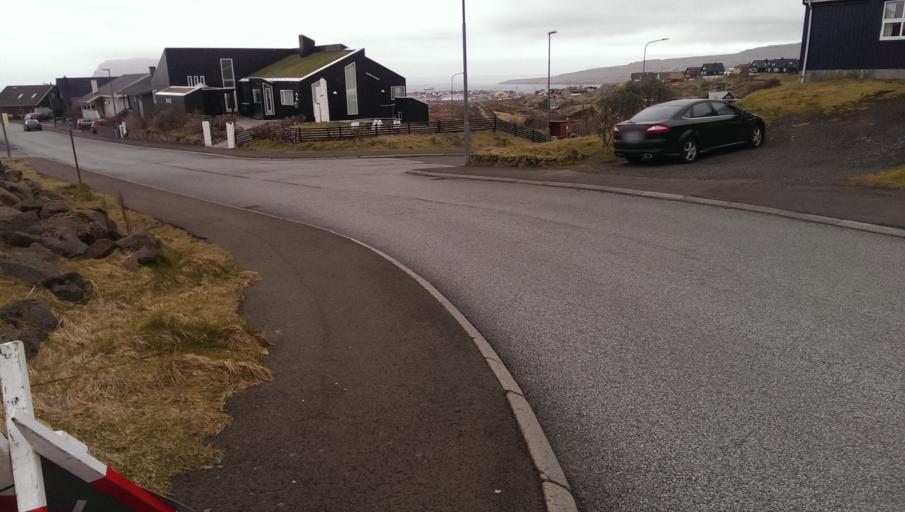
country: FO
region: Streymoy
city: Hoyvik
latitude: 62.0338
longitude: -6.7917
